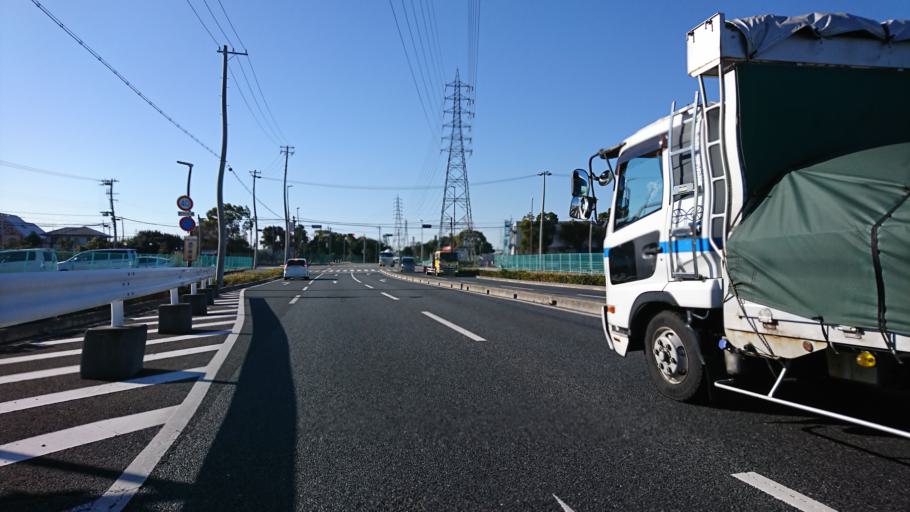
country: JP
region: Hyogo
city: Kakogawacho-honmachi
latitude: 34.7536
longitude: 134.7937
